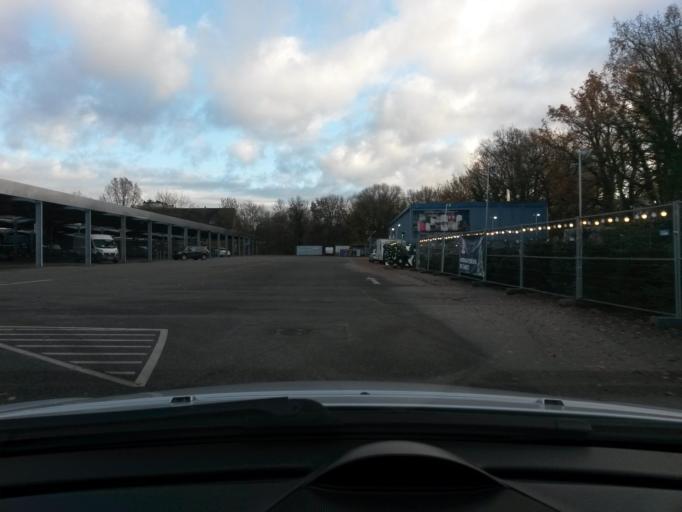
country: DE
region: Hamburg
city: Farmsen-Berne
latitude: 53.6195
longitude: 10.1537
